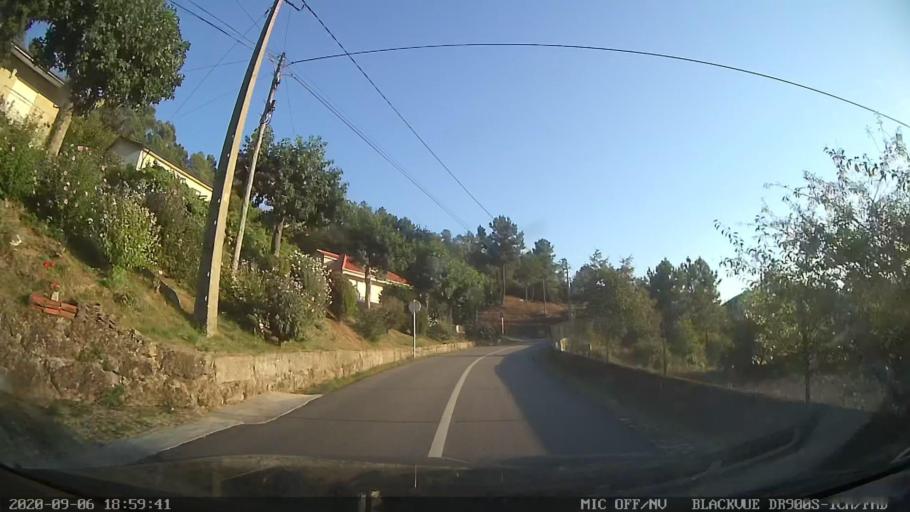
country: PT
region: Porto
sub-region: Baiao
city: Baiao
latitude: 41.2416
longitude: -7.9962
